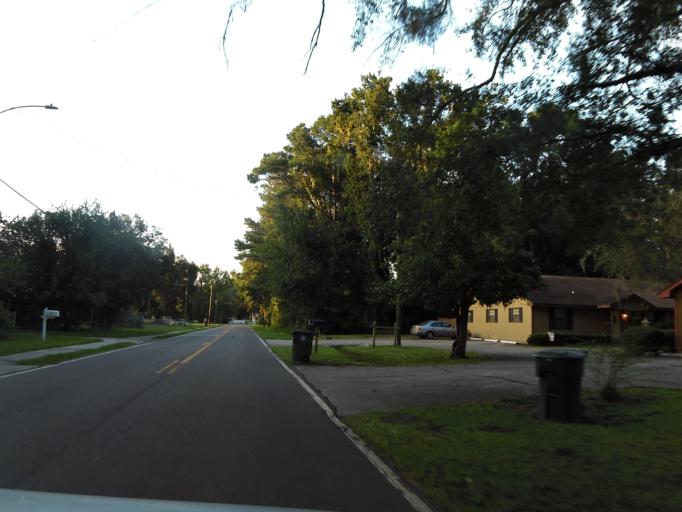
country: US
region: Georgia
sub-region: Camden County
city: Kingsland
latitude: 30.7967
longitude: -81.6942
